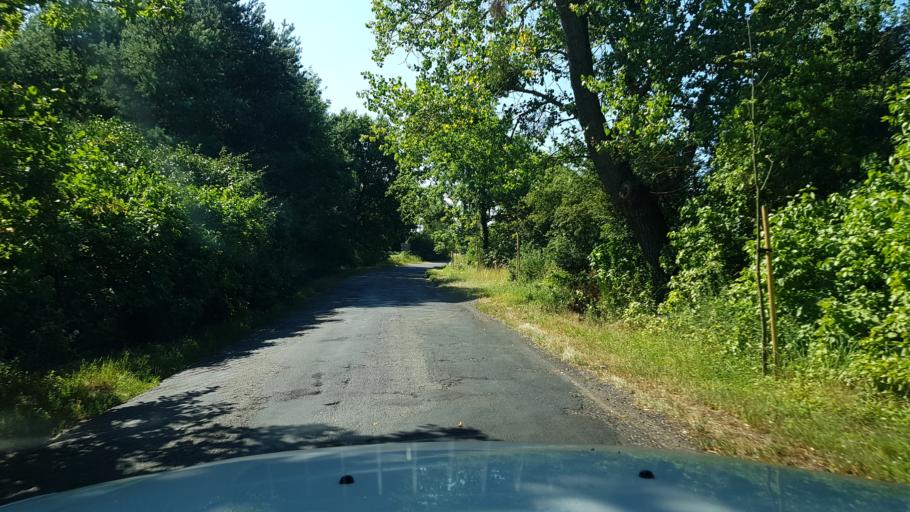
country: PL
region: West Pomeranian Voivodeship
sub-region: Powiat goleniowski
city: Goleniow
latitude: 53.4654
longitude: 14.7147
